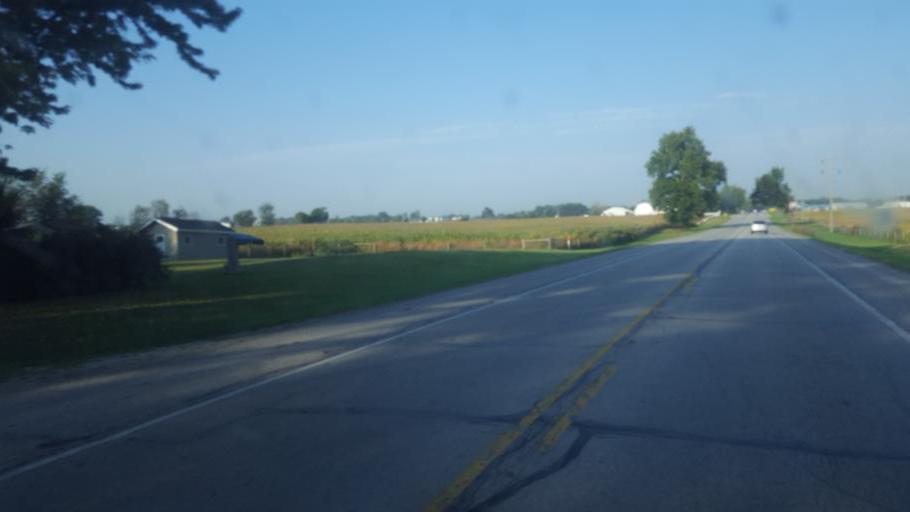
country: US
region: Indiana
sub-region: LaGrange County
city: Topeka
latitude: 41.6405
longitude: -85.5335
